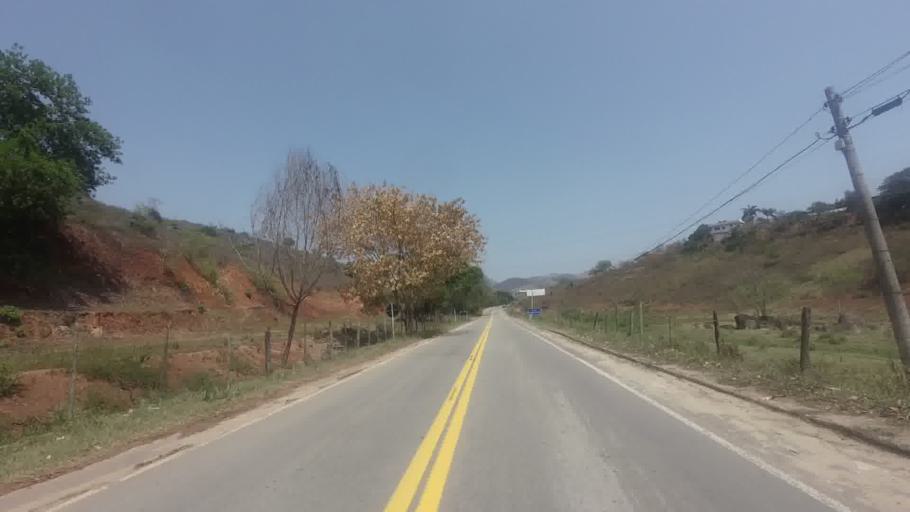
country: BR
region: Espirito Santo
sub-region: Cachoeiro De Itapemirim
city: Cachoeiro de Itapemirim
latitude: -20.8522
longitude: -41.0896
